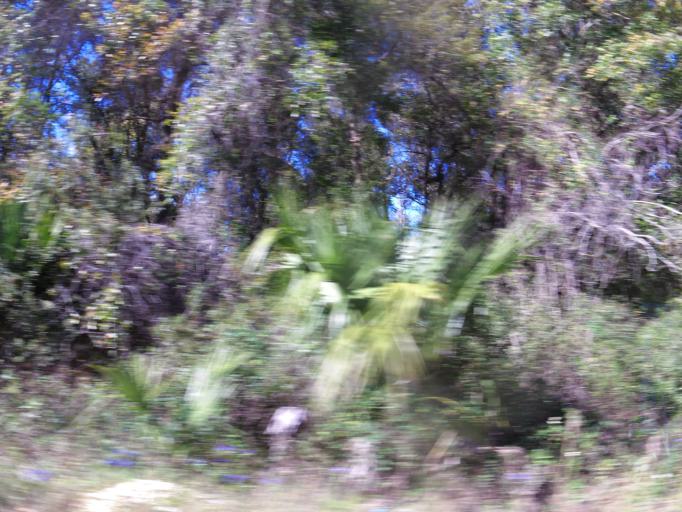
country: US
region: Florida
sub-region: Duval County
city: Jacksonville
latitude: 30.3765
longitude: -81.6429
